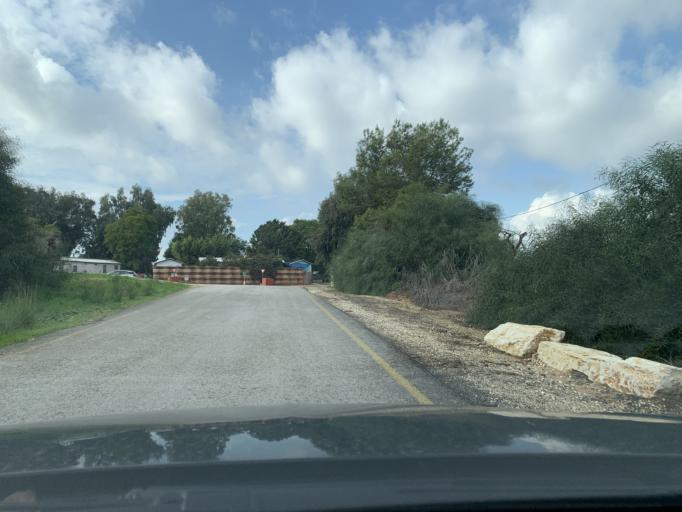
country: PS
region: West Bank
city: Qalqilyah
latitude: 32.1976
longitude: 34.9522
